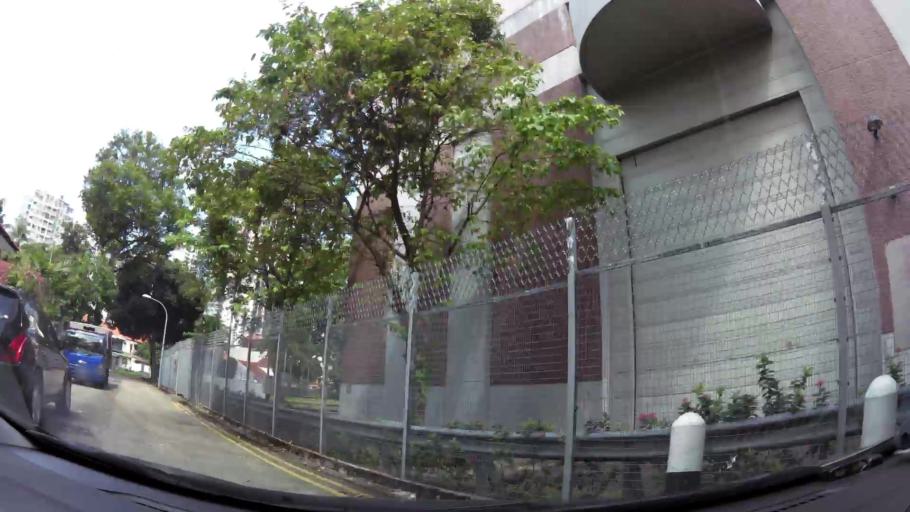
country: SG
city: Singapore
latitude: 1.3124
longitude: 103.8439
